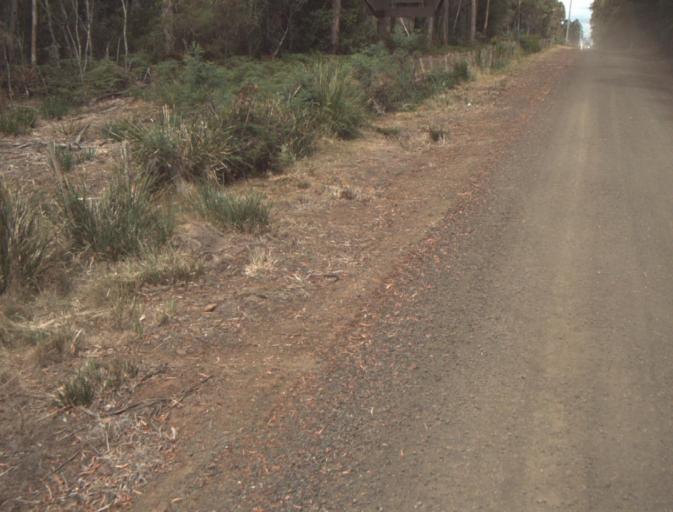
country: AU
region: Tasmania
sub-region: Launceston
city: Mayfield
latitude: -41.2762
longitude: 147.0488
